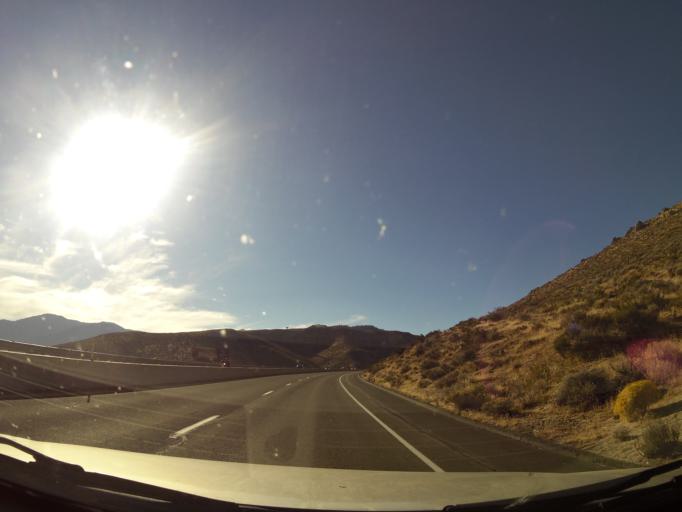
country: US
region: Nevada
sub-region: Douglas County
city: Indian Hills
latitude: 39.1137
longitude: -119.7860
